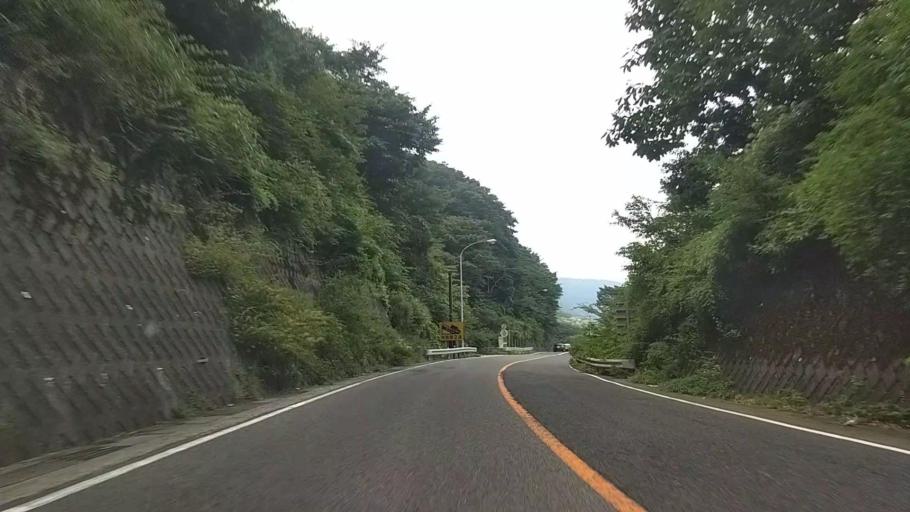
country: JP
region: Kanagawa
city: Hakone
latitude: 35.1981
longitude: 139.0527
